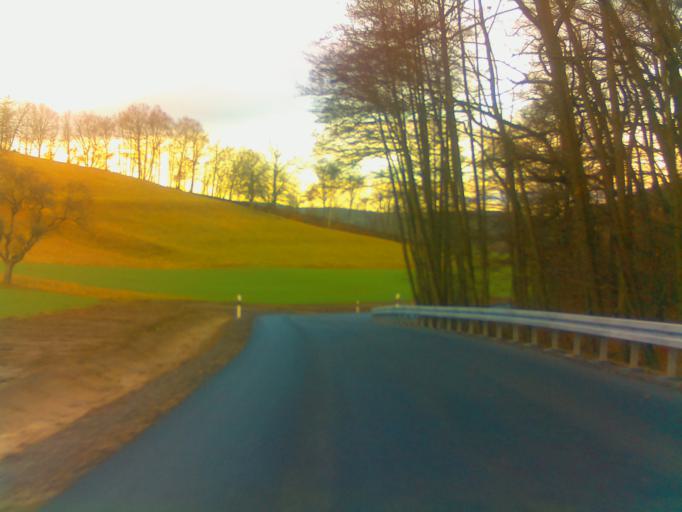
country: DE
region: Thuringia
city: Unterwellenborn
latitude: 50.6862
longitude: 11.4050
